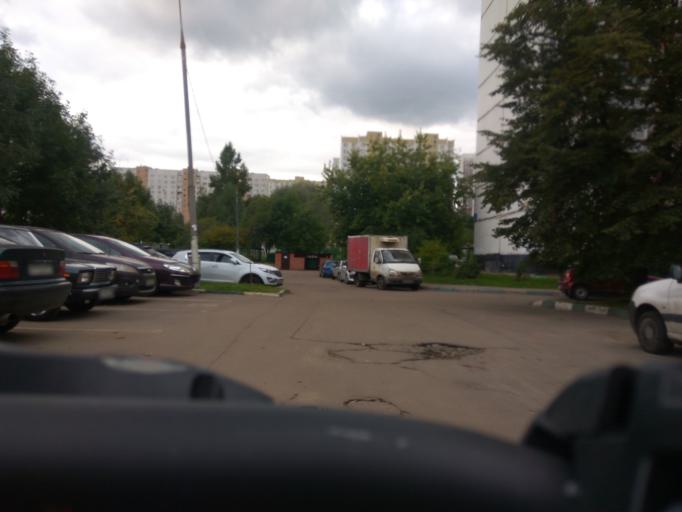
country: RU
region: Moscow
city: Tsaritsyno
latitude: 55.6428
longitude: 37.6589
